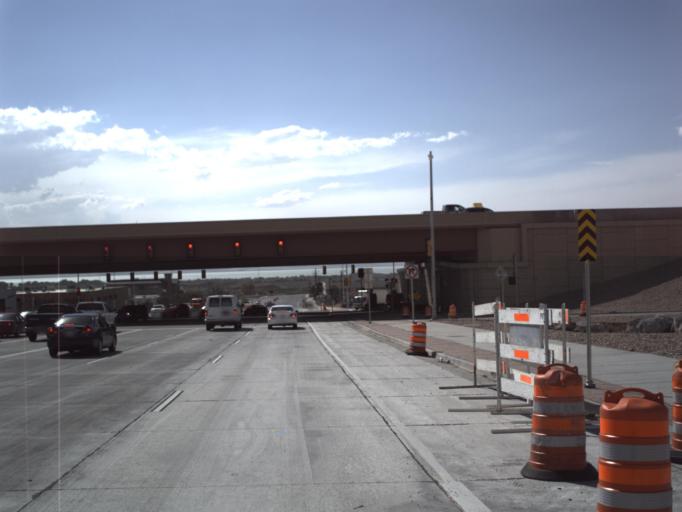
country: US
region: Utah
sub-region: Utah County
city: Orem
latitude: 40.3121
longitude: -111.7219
